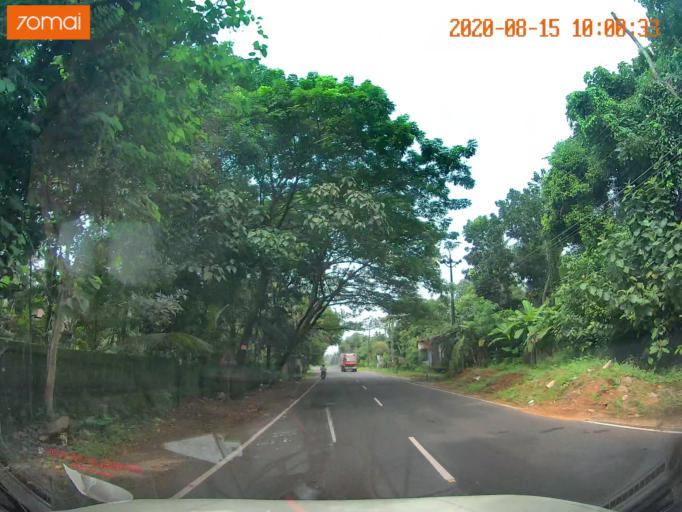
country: IN
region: Kerala
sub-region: Kottayam
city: Changanacheri
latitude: 9.4360
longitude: 76.5490
